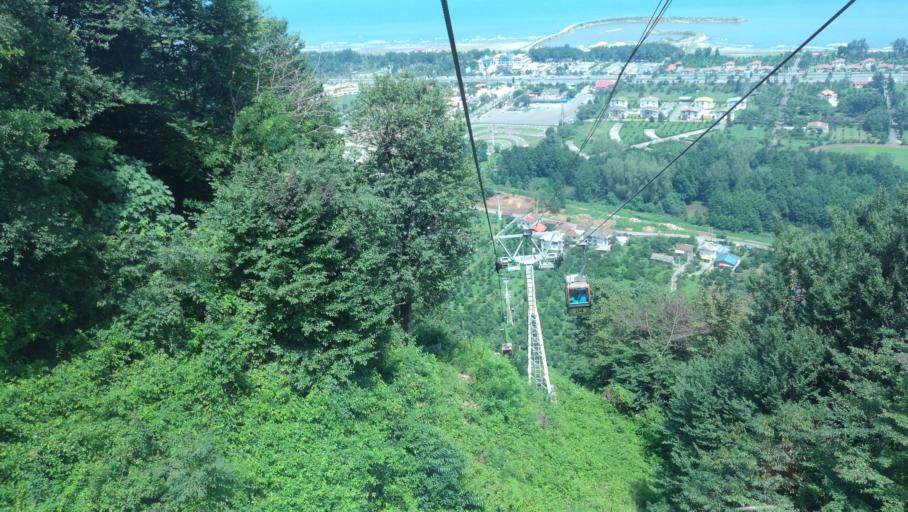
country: IR
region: Mazandaran
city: Ramsar
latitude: 36.9513
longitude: 50.6000
